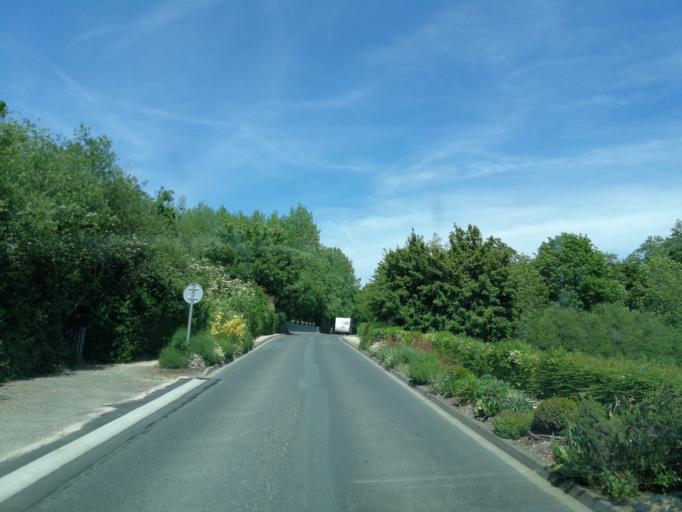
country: FR
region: Poitou-Charentes
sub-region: Departement des Deux-Sevres
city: La Foret-sur-Sevre
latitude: 46.7718
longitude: -0.6475
